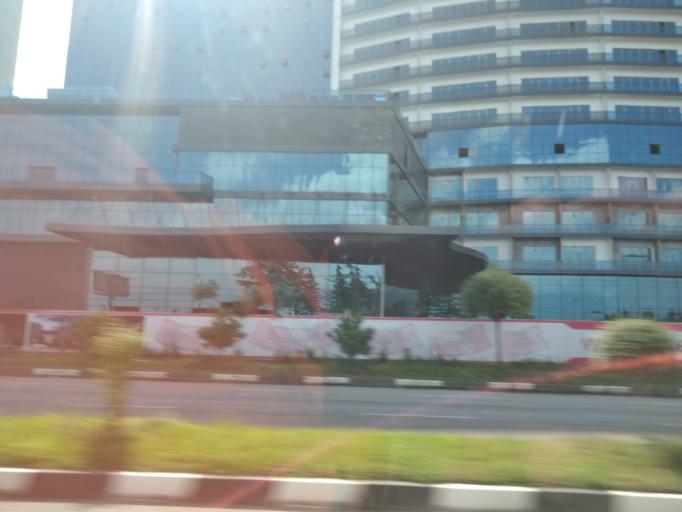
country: GE
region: Ajaria
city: Batumi
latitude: 41.6257
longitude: 41.5981
